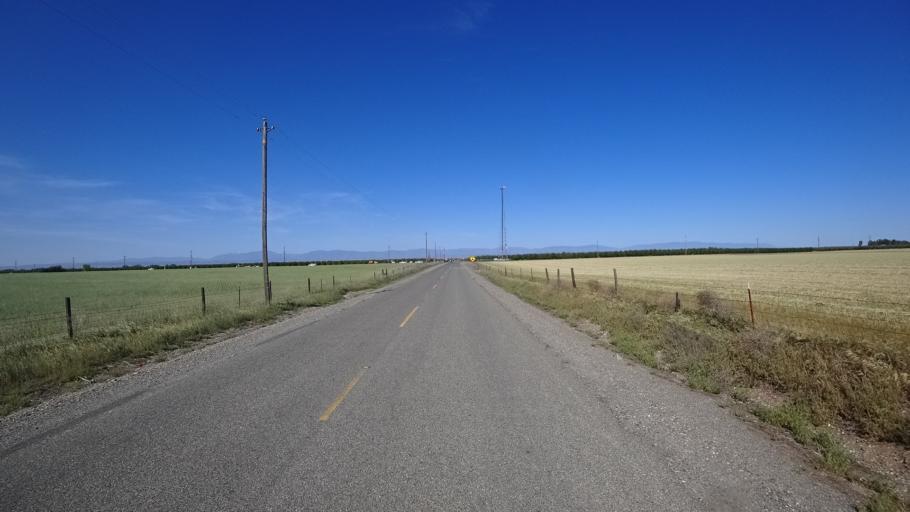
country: US
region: California
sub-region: Glenn County
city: Orland
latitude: 39.6531
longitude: -122.1754
